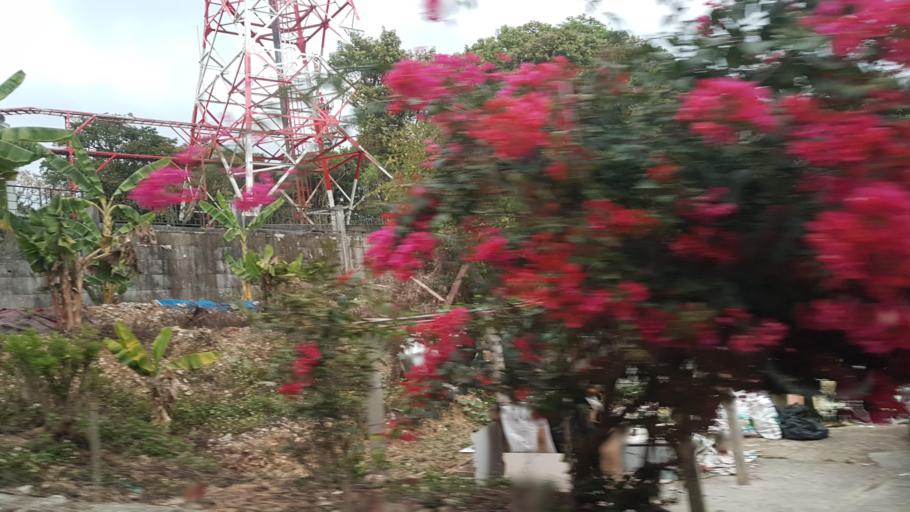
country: TW
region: Taiwan
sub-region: Chiayi
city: Jiayi Shi
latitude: 23.3264
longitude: 120.4872
